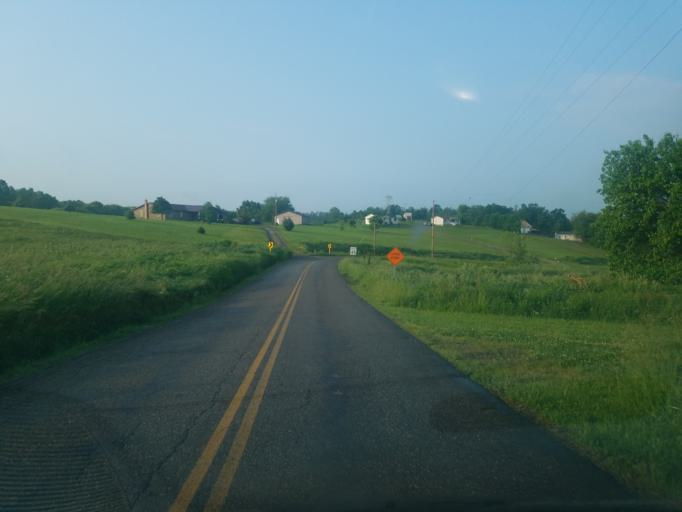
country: US
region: Ohio
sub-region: Stark County
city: Minerva
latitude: 40.6879
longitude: -81.1007
